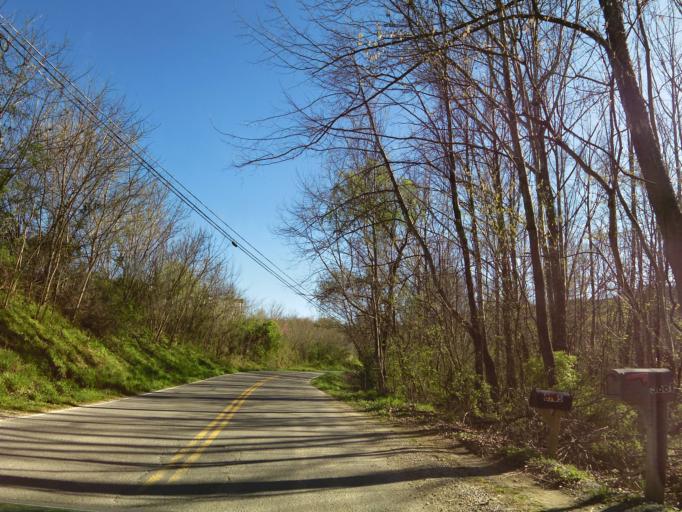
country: US
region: Tennessee
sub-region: Scott County
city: Huntsville
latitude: 36.3392
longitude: -84.3862
